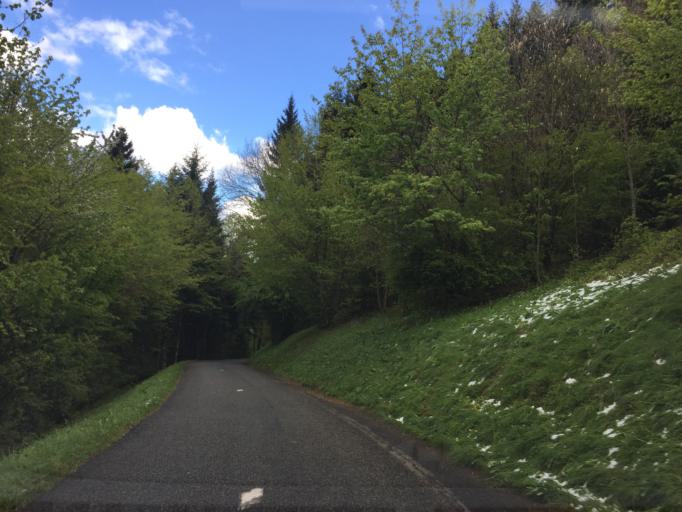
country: FR
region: Rhone-Alpes
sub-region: Departement de la Savoie
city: La Motte-Servolex
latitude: 45.5878
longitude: 5.8295
